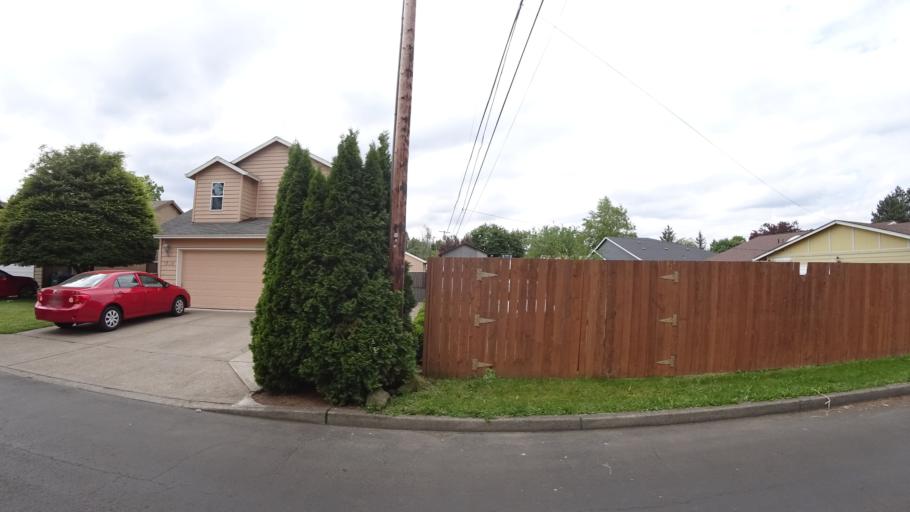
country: US
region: Oregon
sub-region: Multnomah County
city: Gresham
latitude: 45.5100
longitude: -122.4893
